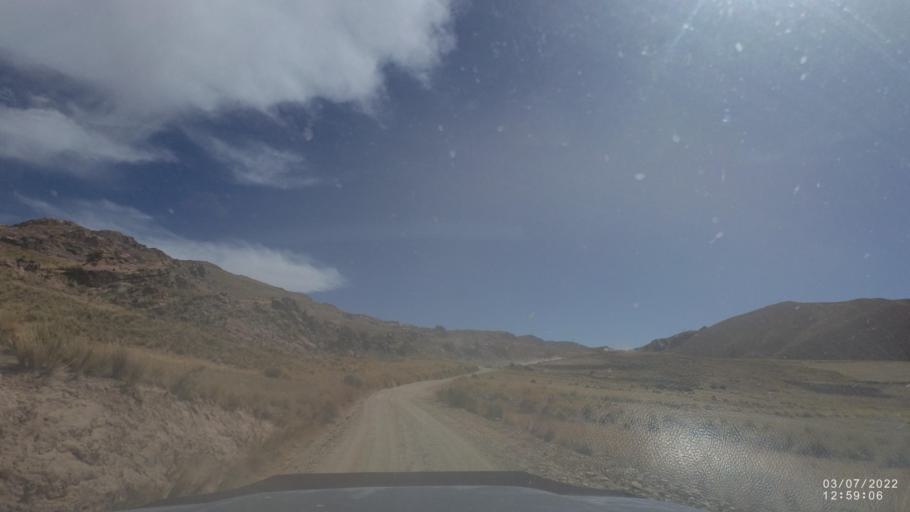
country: BO
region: Cochabamba
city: Sipe Sipe
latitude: -17.7175
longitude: -66.6836
